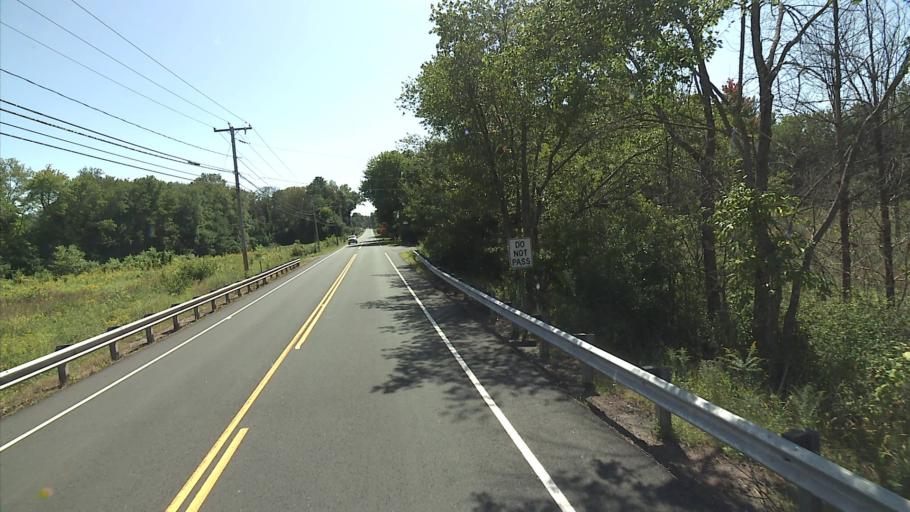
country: US
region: Connecticut
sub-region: Hartford County
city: Windsor Locks
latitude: 41.8952
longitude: -72.6266
